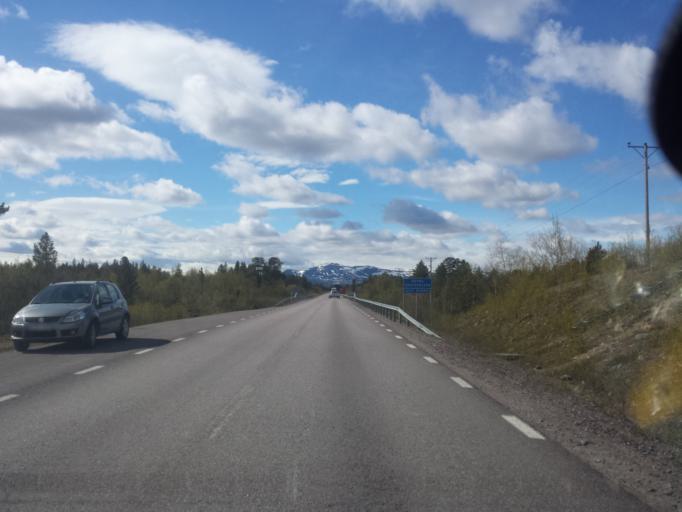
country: SE
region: Norrbotten
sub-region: Kiruna Kommun
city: Kiruna
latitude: 67.9899
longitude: 19.9264
